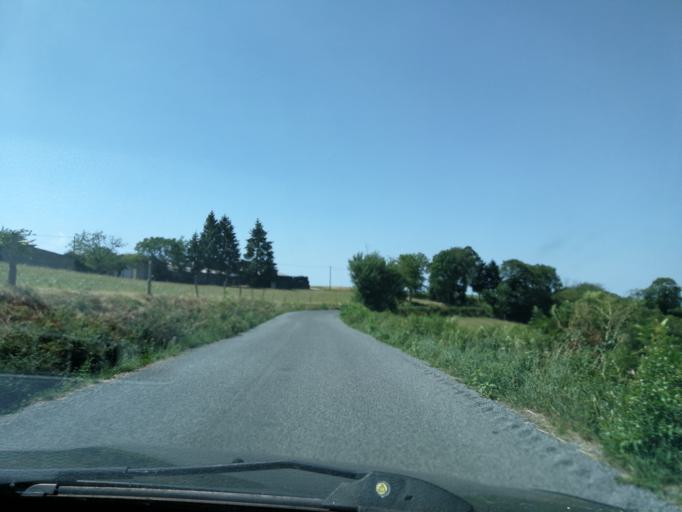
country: FR
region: Midi-Pyrenees
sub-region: Departement de l'Aveyron
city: Livinhac-le-Haut
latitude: 44.6644
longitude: 2.3019
